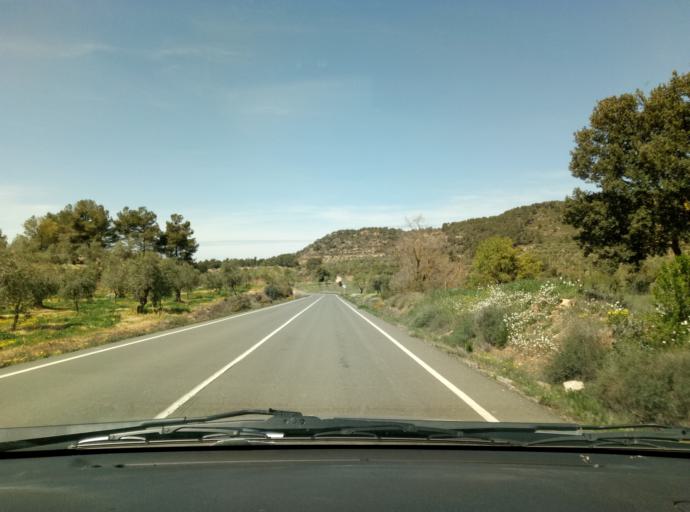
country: ES
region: Catalonia
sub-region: Provincia de Lleida
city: Vinaixa
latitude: 41.4255
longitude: 0.9046
